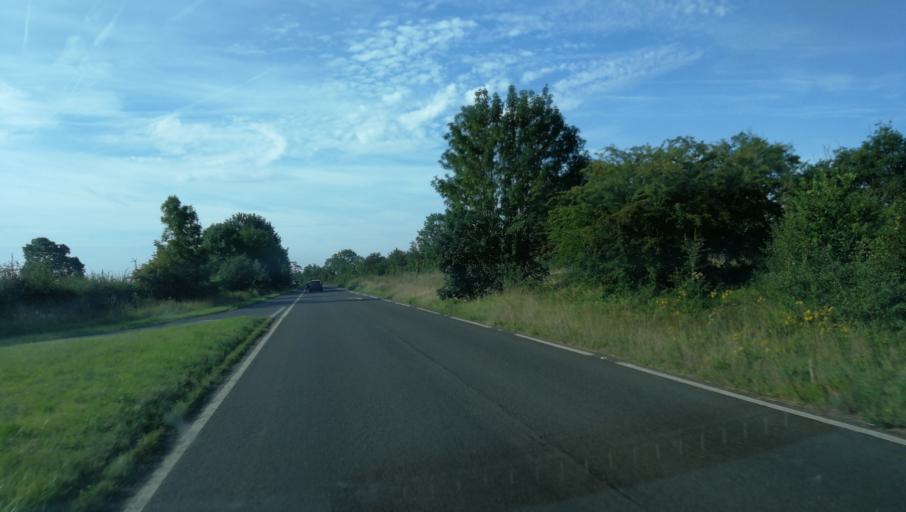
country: GB
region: England
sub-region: Oxfordshire
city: Deddington
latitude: 51.9388
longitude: -1.3265
